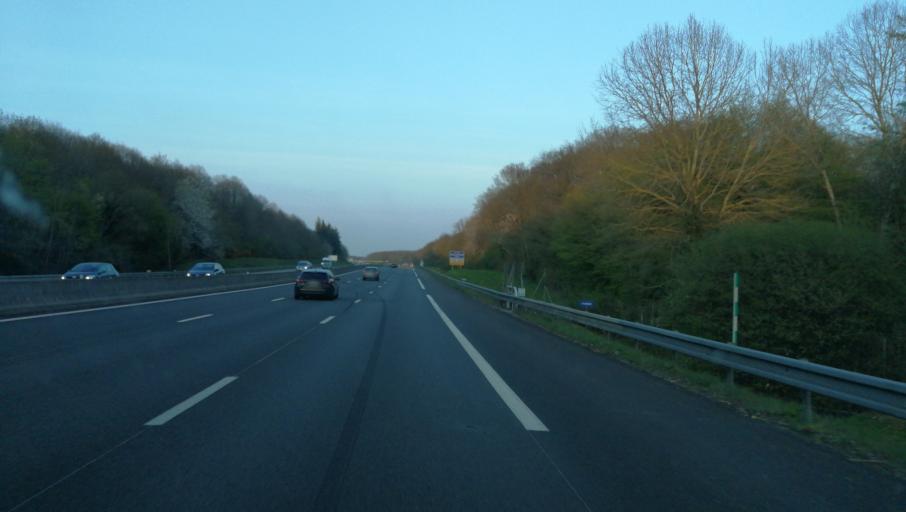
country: FR
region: Centre
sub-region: Departement d'Eure-et-Loir
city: Gasville-Oiseme
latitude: 48.4632
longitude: 1.5599
